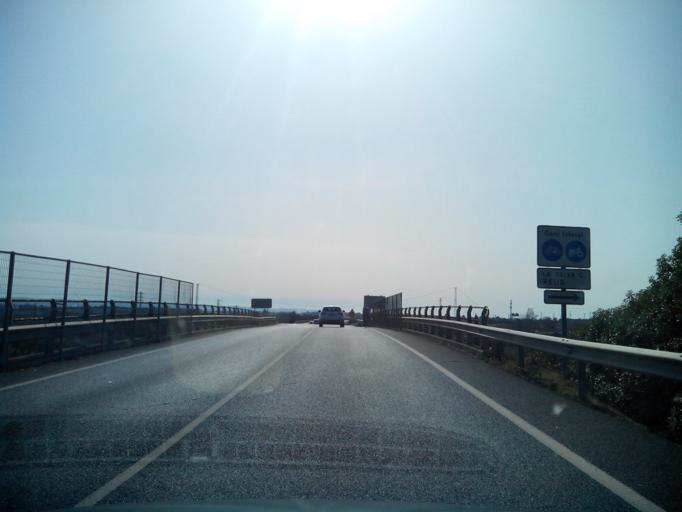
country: ES
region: Catalonia
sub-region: Provincia de Tarragona
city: Alcover
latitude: 41.2666
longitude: 1.1751
